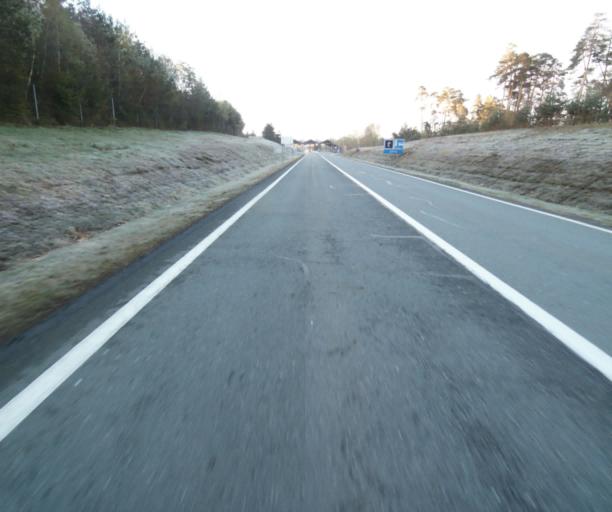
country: FR
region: Limousin
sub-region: Departement de la Correze
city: Correze
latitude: 45.3208
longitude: 1.8500
